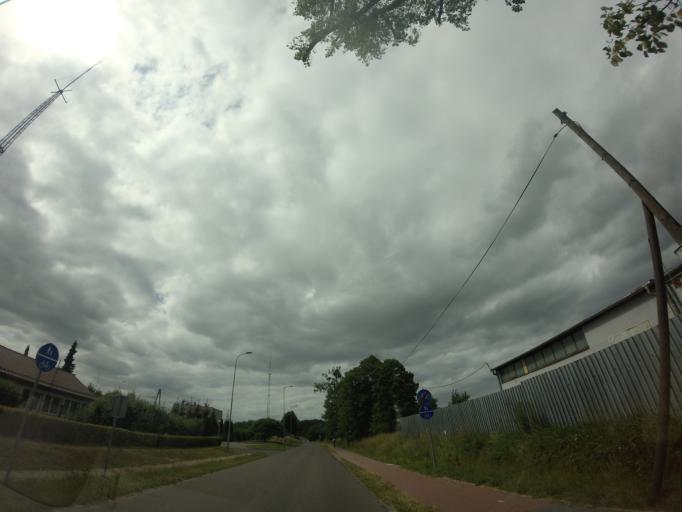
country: PL
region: Lubusz
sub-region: Powiat strzelecko-drezdenecki
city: Strzelce Krajenskie
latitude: 52.8693
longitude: 15.5283
